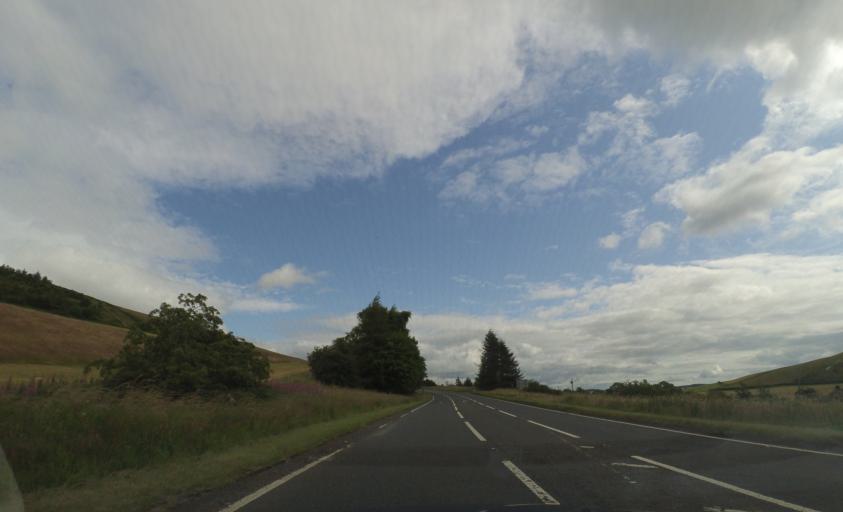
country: GB
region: Scotland
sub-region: The Scottish Borders
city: Selkirk
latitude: 55.4962
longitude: -2.8344
